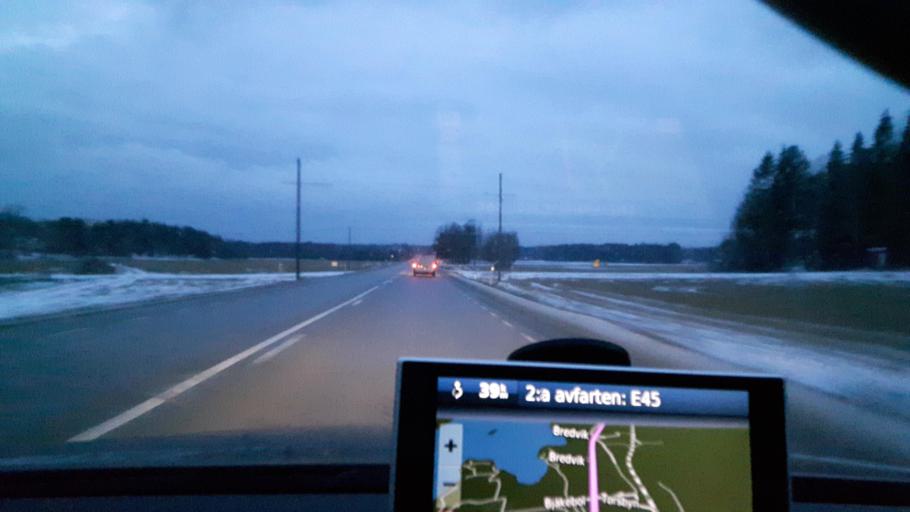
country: SE
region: Vaestra Goetaland
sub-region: Amals Kommun
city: Amal
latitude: 59.0092
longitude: 12.6891
